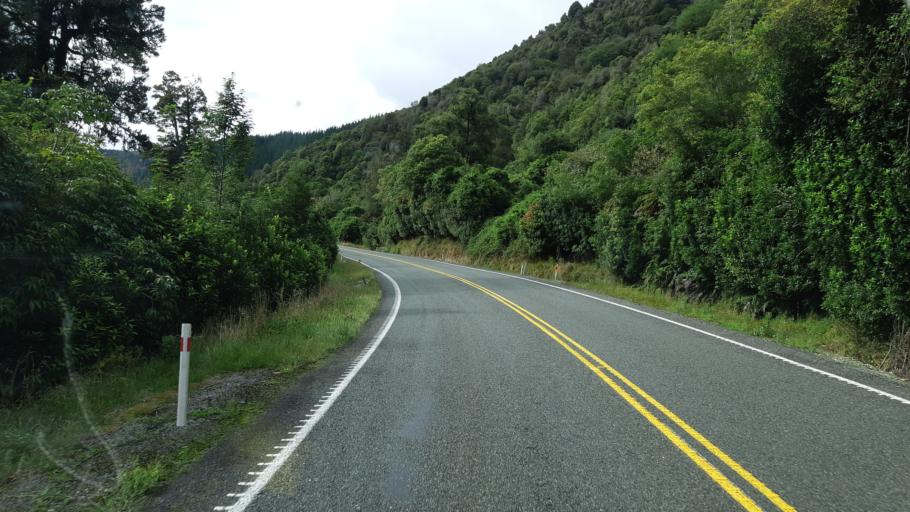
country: NZ
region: West Coast
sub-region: Buller District
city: Westport
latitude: -41.7751
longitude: 172.2403
